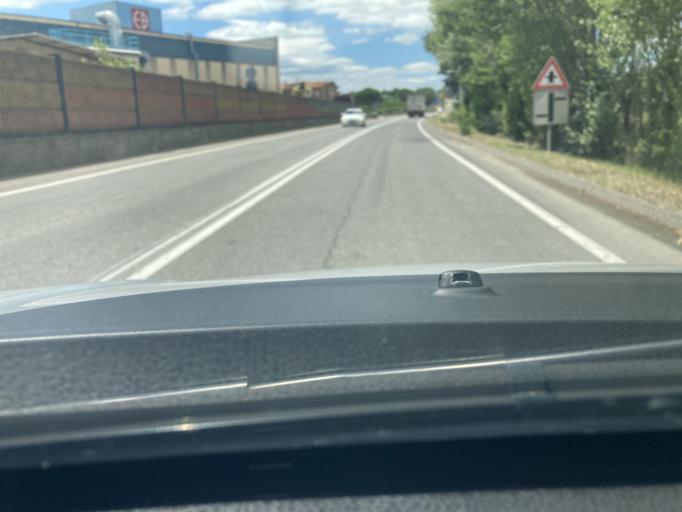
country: IT
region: Umbria
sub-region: Provincia di Perugia
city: Corciano
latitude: 43.1329
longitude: 12.2597
